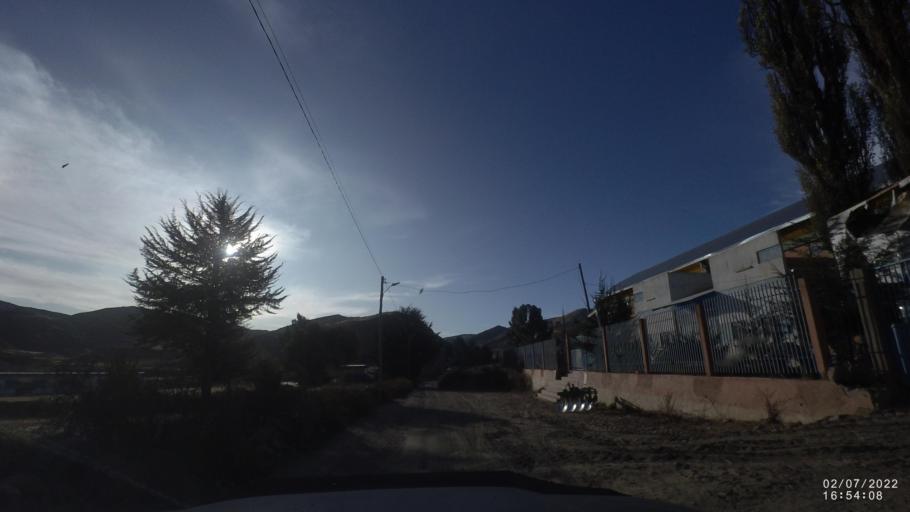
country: BO
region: Cochabamba
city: Irpa Irpa
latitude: -17.9671
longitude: -66.5388
